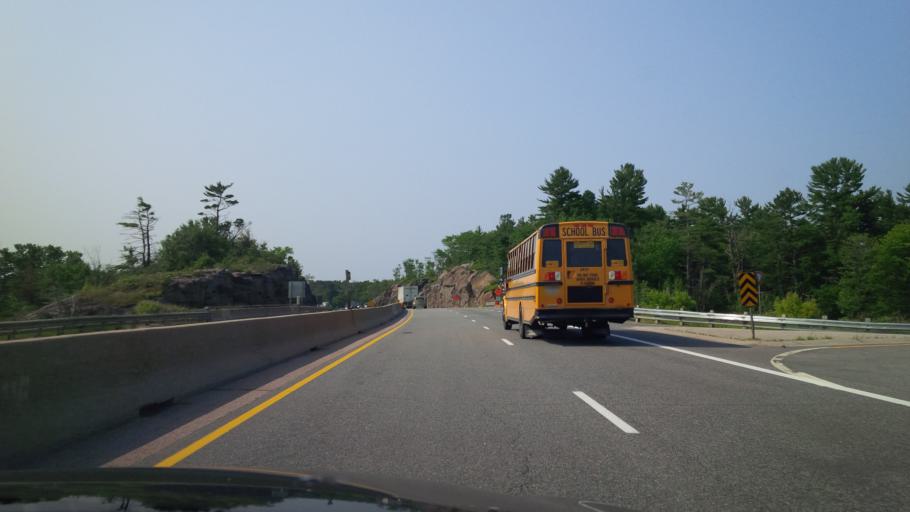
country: CA
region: Ontario
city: Gravenhurst
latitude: 44.7808
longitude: -79.3348
